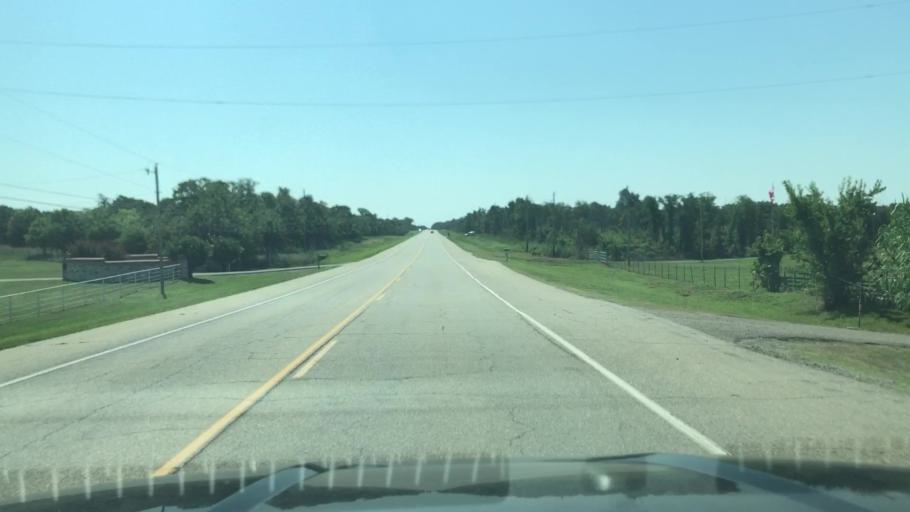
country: US
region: Oklahoma
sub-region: Creek County
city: Mannford
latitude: 35.9962
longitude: -96.3600
